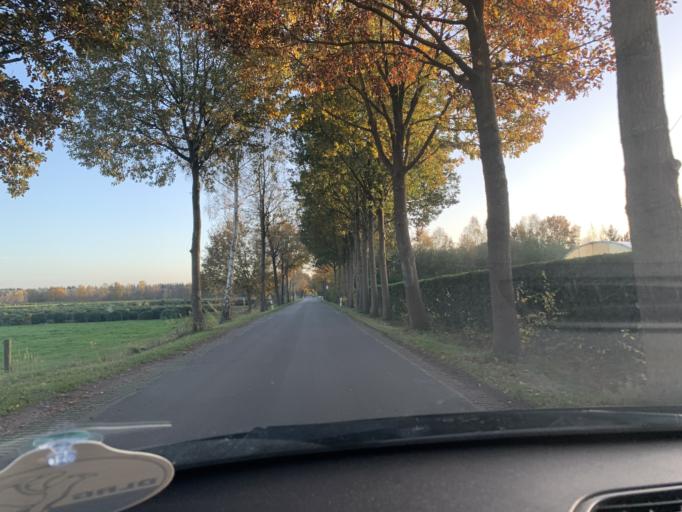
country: DE
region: Lower Saxony
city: Bad Zwischenahn
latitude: 53.1438
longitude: 8.0455
